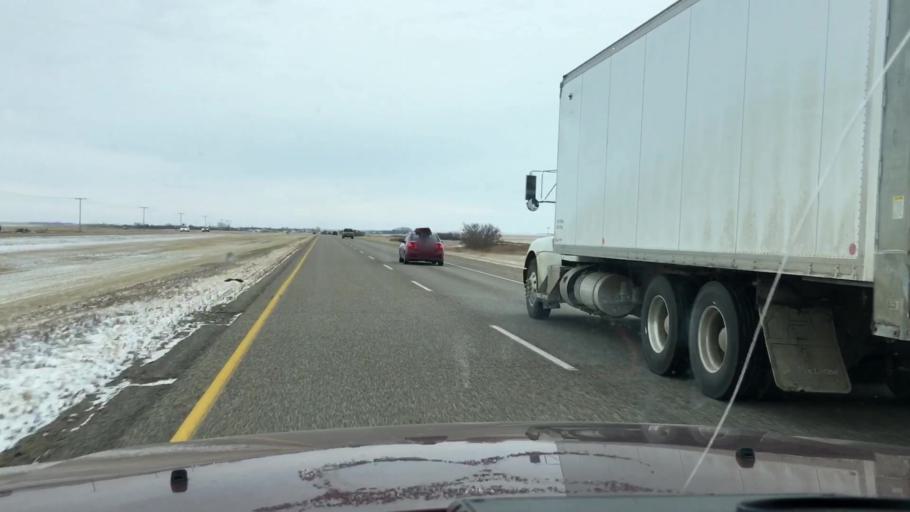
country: CA
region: Saskatchewan
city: Watrous
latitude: 51.1777
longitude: -105.9368
